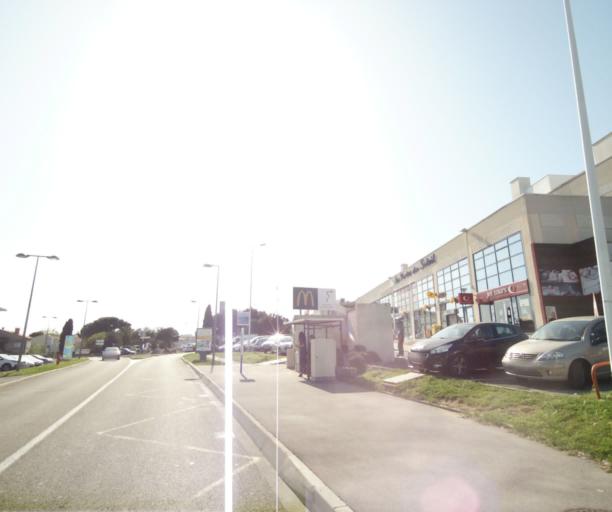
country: FR
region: Languedoc-Roussillon
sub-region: Departement de l'Herault
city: Juvignac
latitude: 43.6128
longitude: 3.8089
